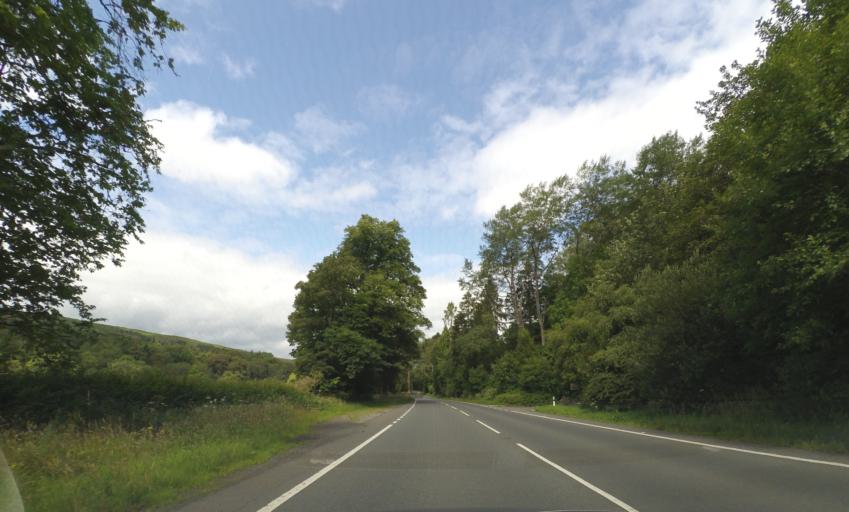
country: GB
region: Scotland
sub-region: The Scottish Borders
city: Selkirk
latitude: 55.6084
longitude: -2.9018
